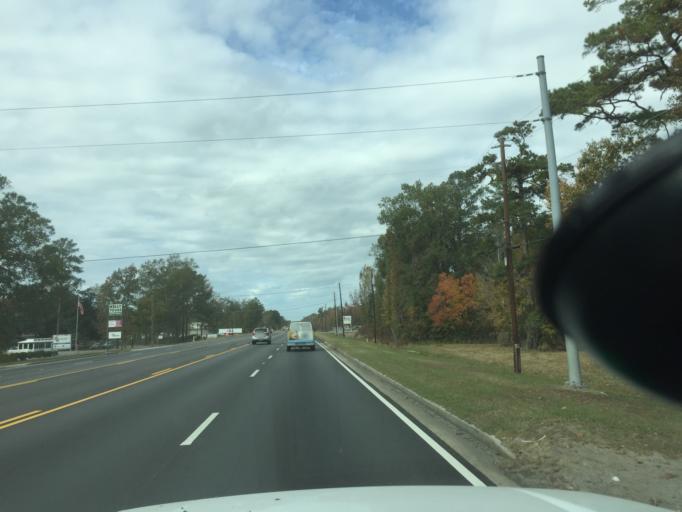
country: US
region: Georgia
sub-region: Chatham County
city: Garden City
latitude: 32.0895
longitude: -81.1818
